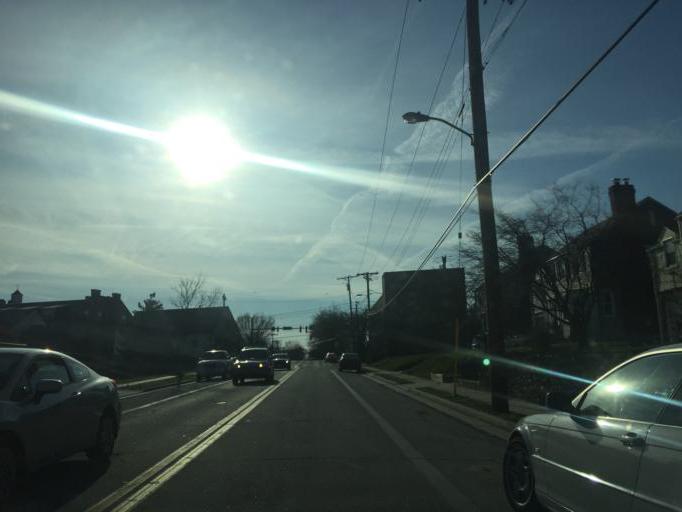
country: US
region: Maryland
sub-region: Baltimore County
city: Towson
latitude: 39.3840
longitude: -76.6055
